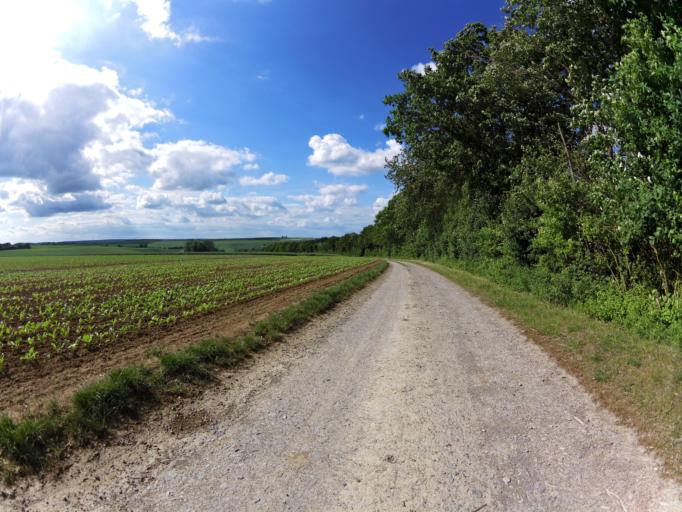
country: DE
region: Bavaria
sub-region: Regierungsbezirk Unterfranken
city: Gaukonigshofen
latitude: 49.6620
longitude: 10.0239
